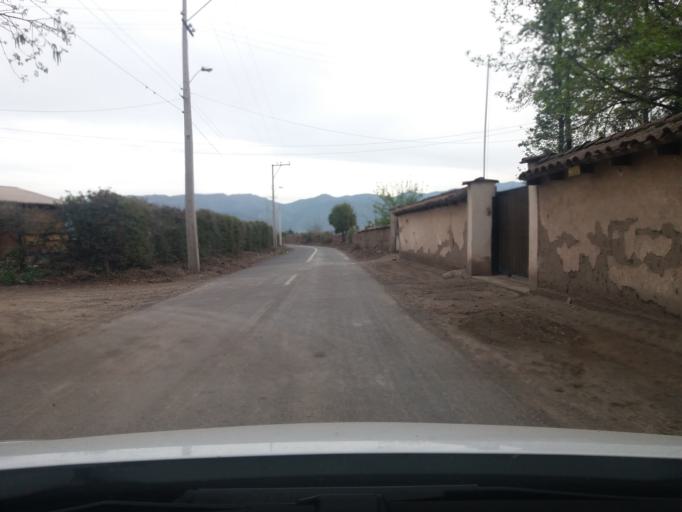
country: CL
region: Valparaiso
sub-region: Provincia de Los Andes
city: Los Andes
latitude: -32.8503
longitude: -70.6341
